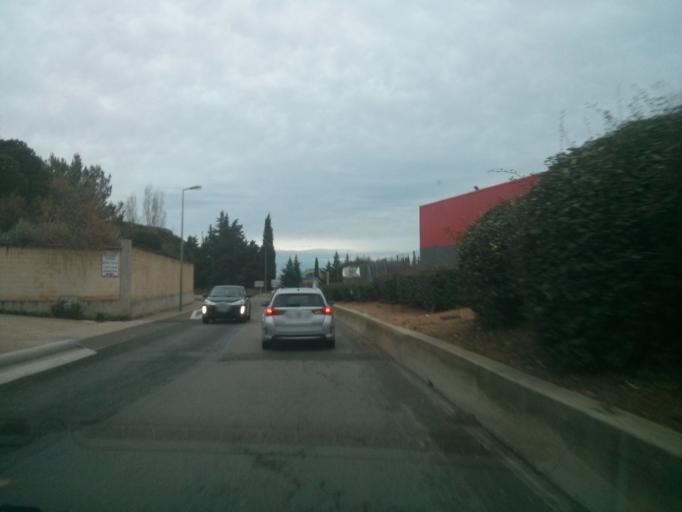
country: FR
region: Languedoc-Roussillon
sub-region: Departement du Gard
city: Saint-Gilles
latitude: 43.6722
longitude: 4.4223
